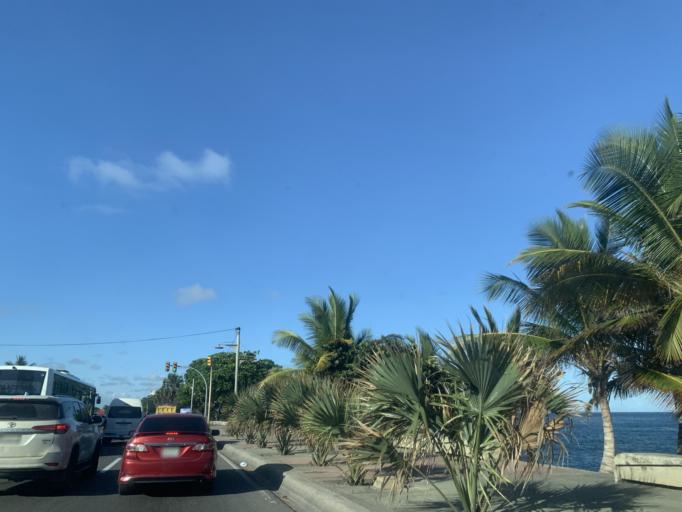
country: DO
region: Nacional
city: Bella Vista
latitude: 18.4436
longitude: -69.9273
